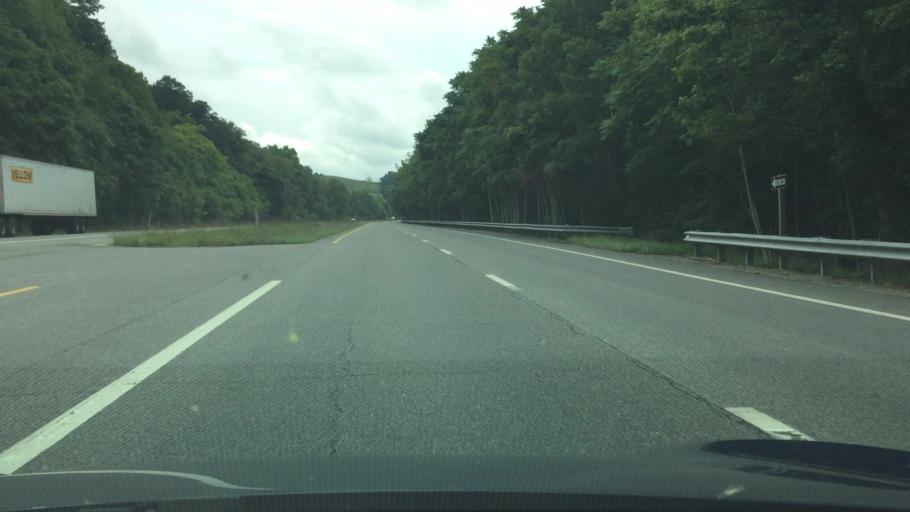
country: US
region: Virginia
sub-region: City of Radford
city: Radford
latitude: 37.1123
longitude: -80.5250
